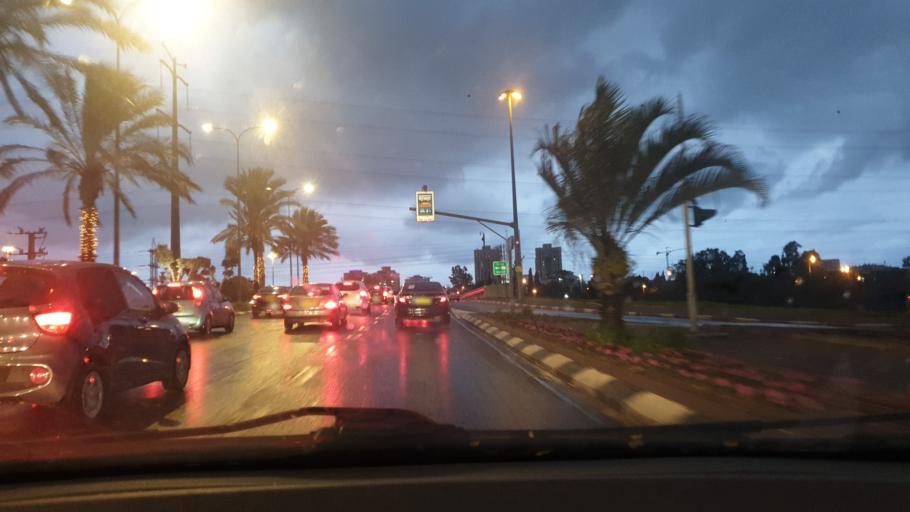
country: IL
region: Central District
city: Rishon LeZiyyon
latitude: 31.9771
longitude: 34.7938
